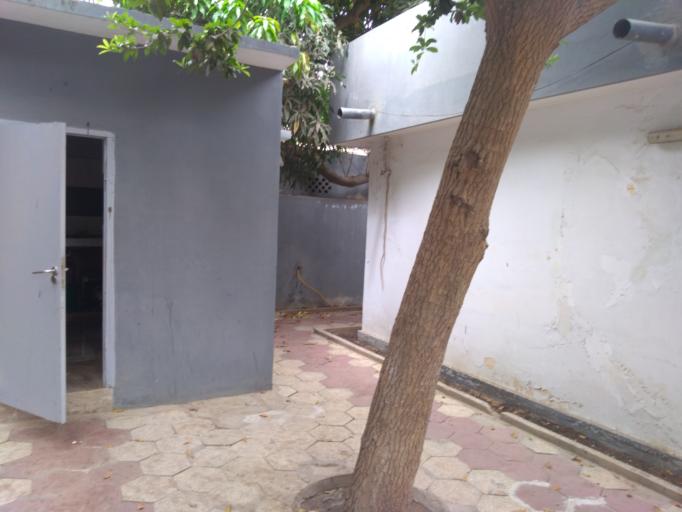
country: SN
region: Dakar
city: Grand Dakar
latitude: 14.7212
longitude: -17.4604
